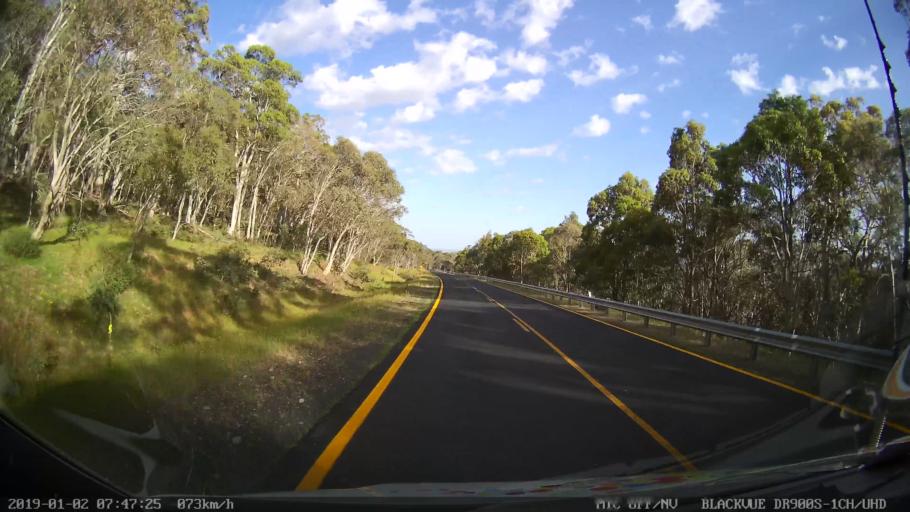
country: AU
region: New South Wales
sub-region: Tumut Shire
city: Tumut
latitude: -35.7650
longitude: 148.5208
